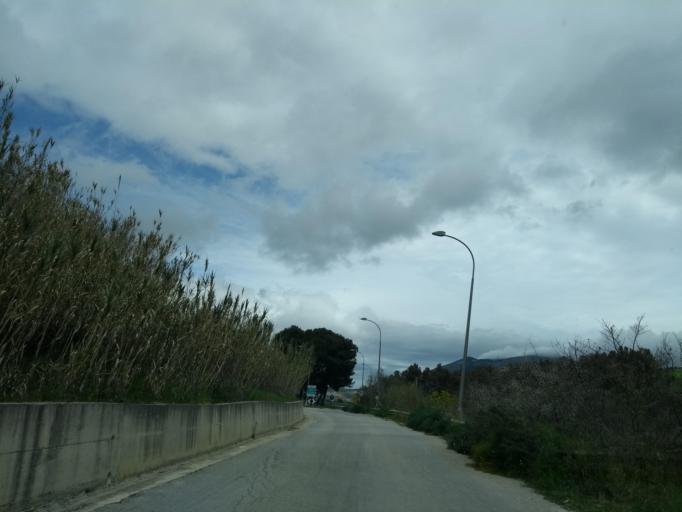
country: IT
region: Sicily
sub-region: Trapani
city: Calatafimi
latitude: 37.9453
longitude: 12.8323
